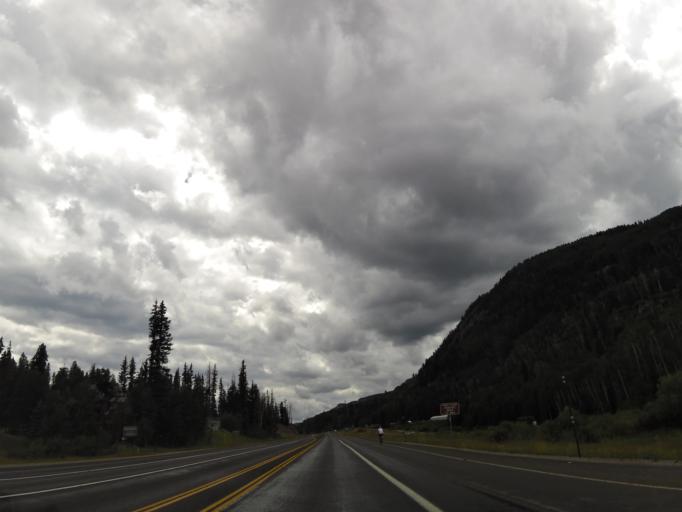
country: US
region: Colorado
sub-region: San Juan County
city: Silverton
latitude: 37.6268
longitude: -107.8105
